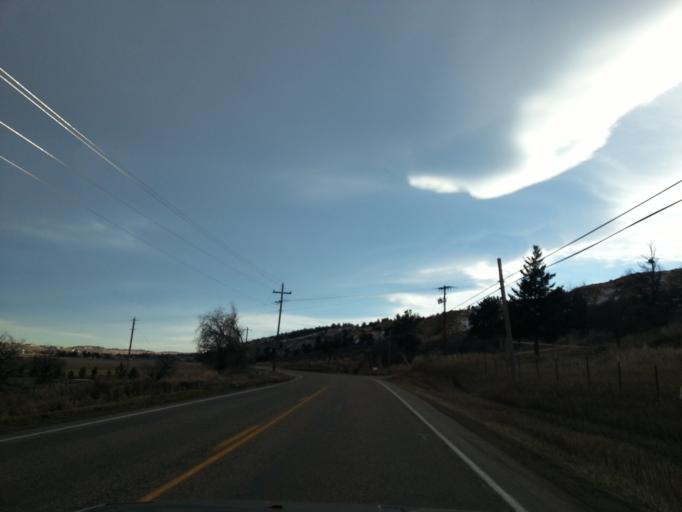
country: US
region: Colorado
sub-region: Larimer County
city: Loveland
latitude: 40.4522
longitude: -105.2047
